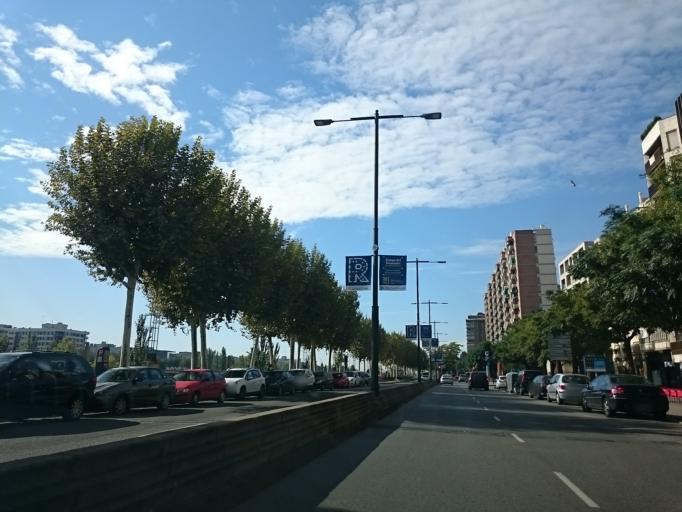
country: ES
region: Catalonia
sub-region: Provincia de Lleida
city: Lleida
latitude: 41.6125
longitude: 0.6247
